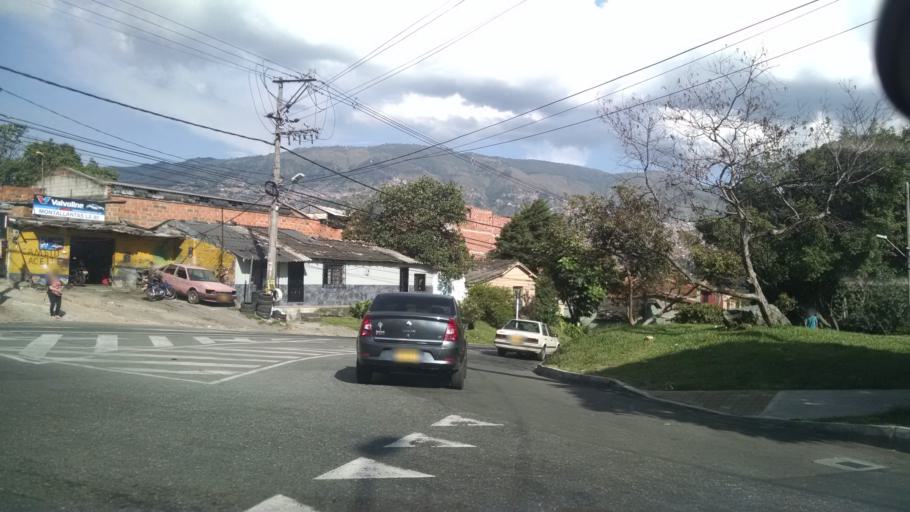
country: CO
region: Antioquia
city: Medellin
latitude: 6.2802
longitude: -75.5791
